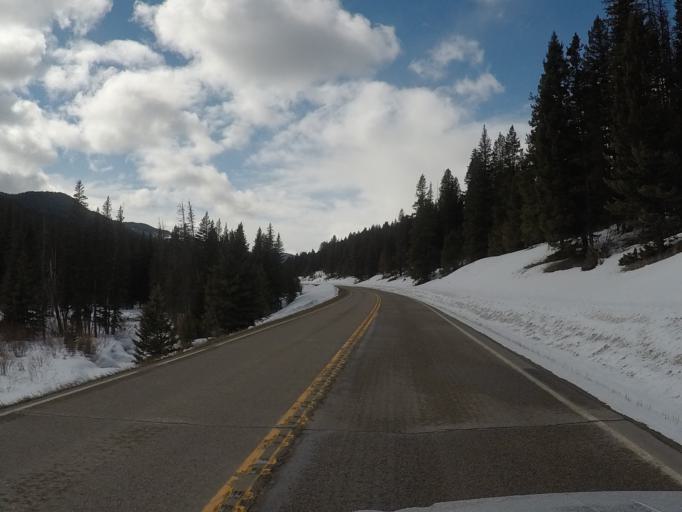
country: US
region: Montana
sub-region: Meagher County
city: White Sulphur Springs
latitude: 46.7601
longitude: -110.7233
